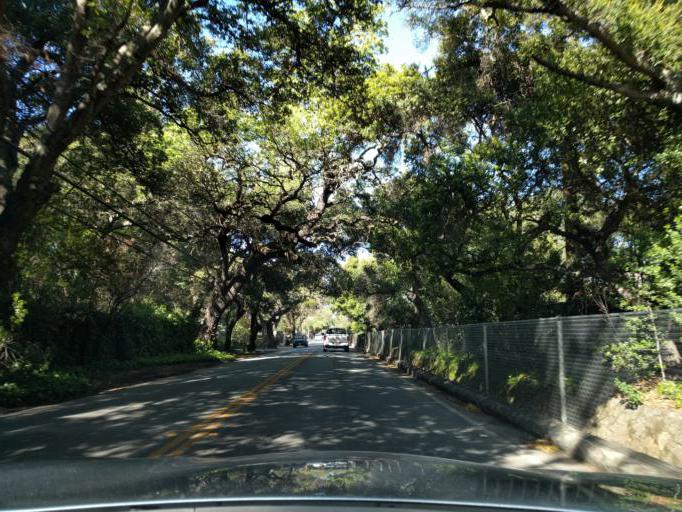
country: US
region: California
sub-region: San Mateo County
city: North Fair Oaks
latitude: 37.4707
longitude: -122.1902
